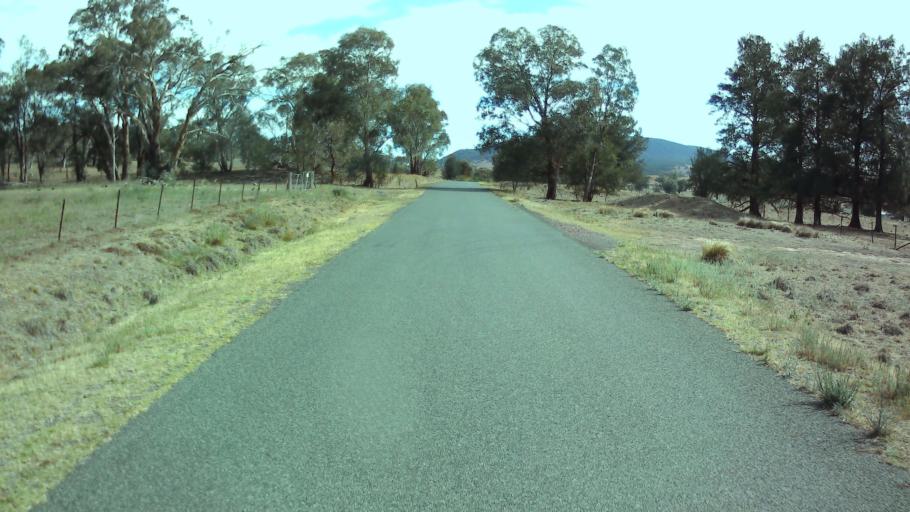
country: AU
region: New South Wales
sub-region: Weddin
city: Grenfell
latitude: -33.8121
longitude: 148.2925
